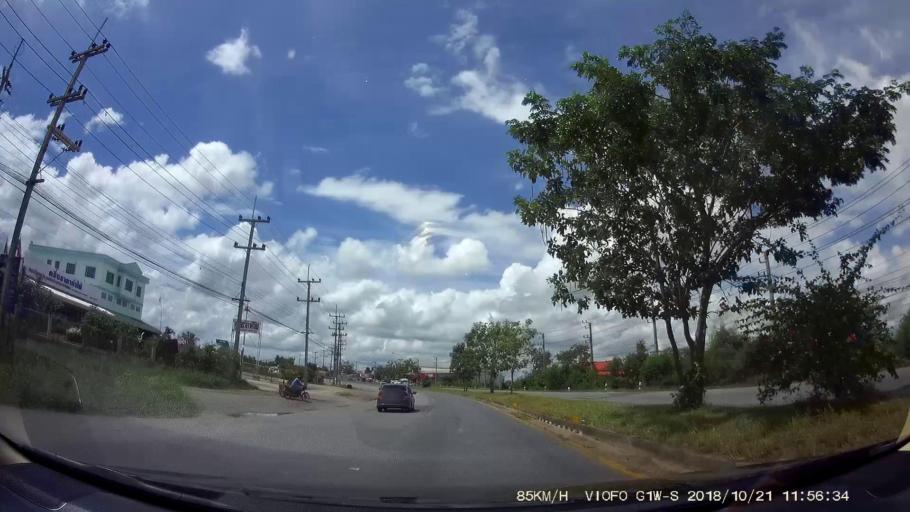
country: TH
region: Chaiyaphum
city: Chatturat
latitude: 15.5790
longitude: 101.8741
